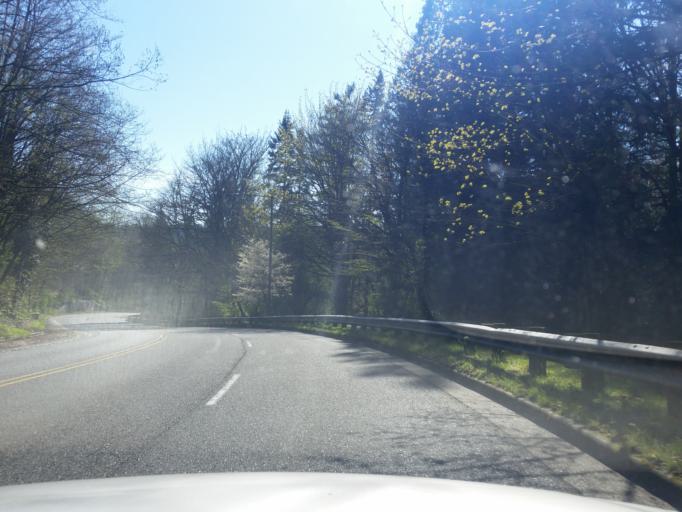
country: US
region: Washington
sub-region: Snohomish County
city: Mill Creek
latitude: 47.8515
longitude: -122.2129
